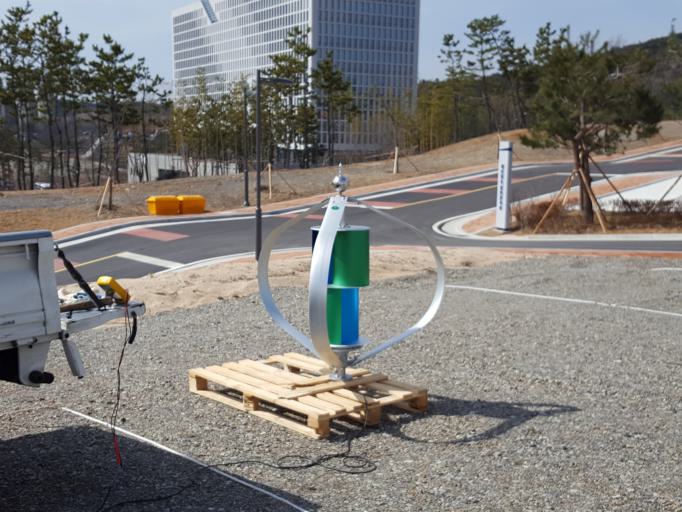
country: KR
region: Ulsan
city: Ulsan
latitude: 35.5657
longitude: 129.3164
